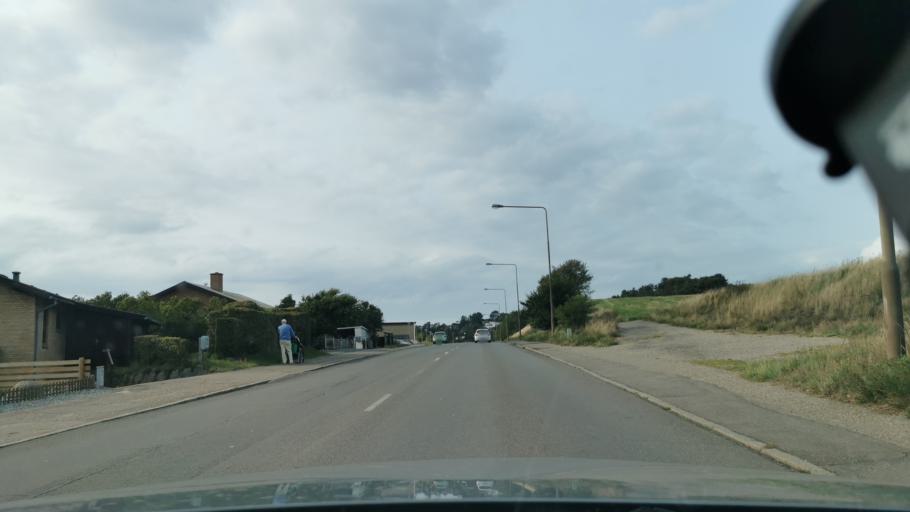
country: DK
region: Zealand
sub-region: Kalundborg Kommune
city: Kalundborg
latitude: 55.6902
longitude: 11.0533
